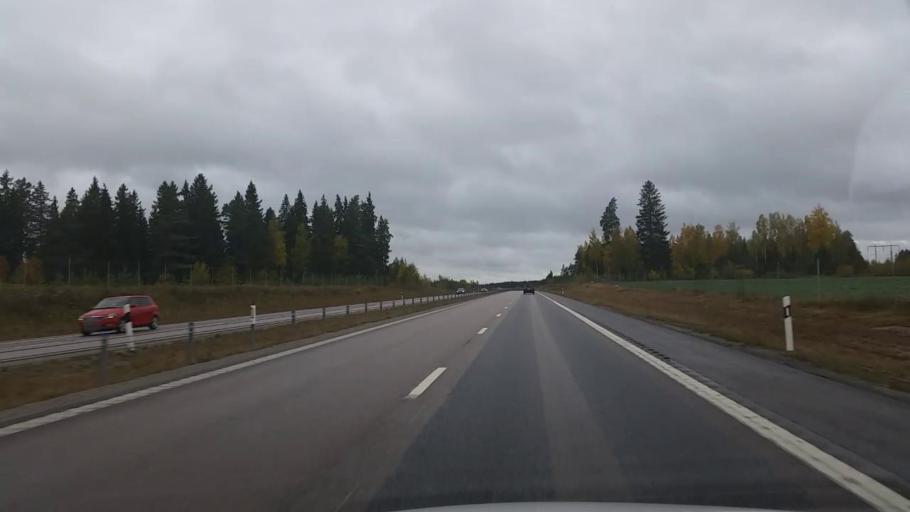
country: SE
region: Uppsala
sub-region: Osthammars Kommun
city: Bjorklinge
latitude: 60.1073
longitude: 17.5590
